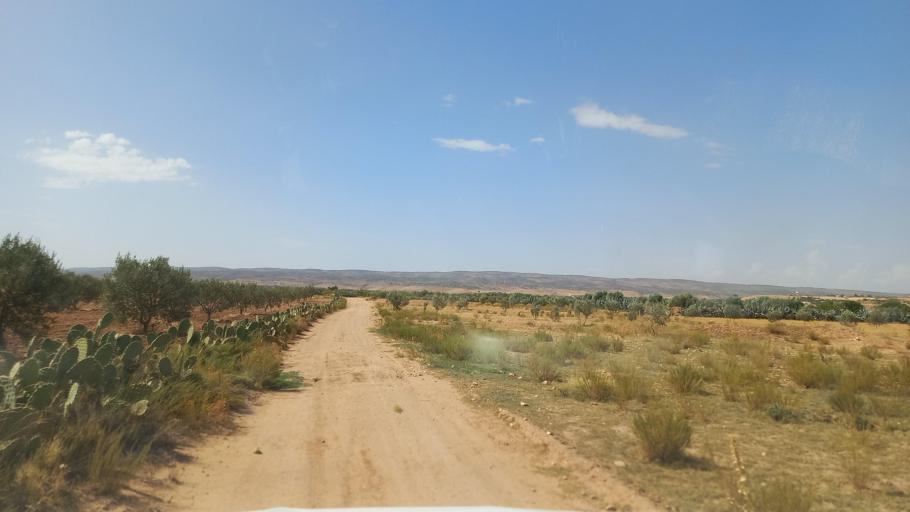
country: TN
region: Al Qasrayn
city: Kasserine
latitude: 35.2569
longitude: 8.9546
